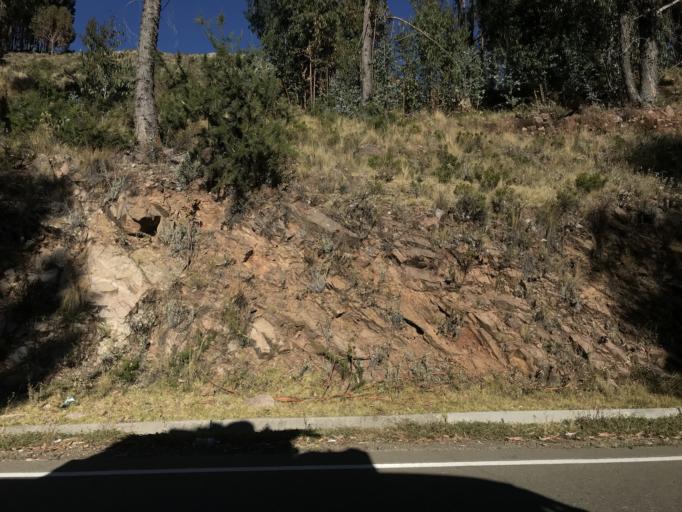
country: BO
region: La Paz
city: San Pedro
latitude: -16.2246
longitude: -68.8545
